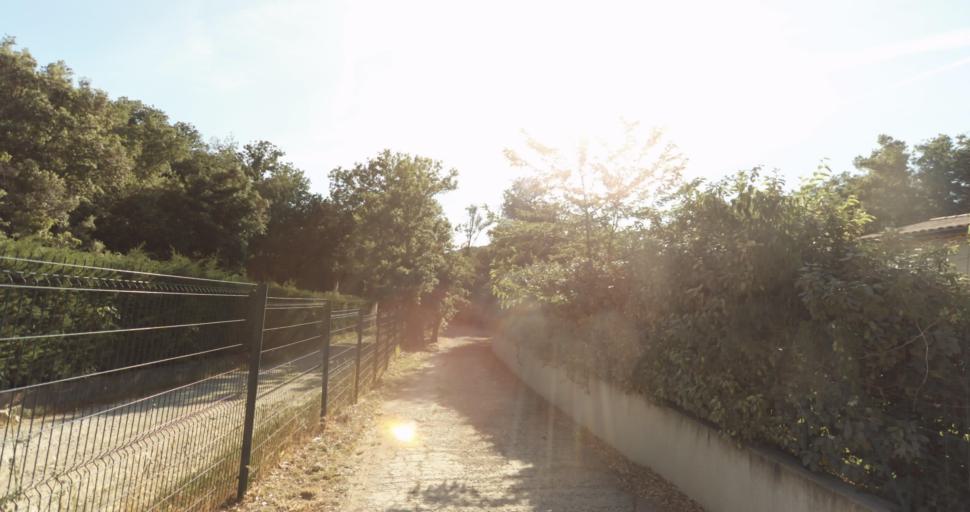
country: FR
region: Provence-Alpes-Cote d'Azur
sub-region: Departement du Var
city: Gassin
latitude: 43.2243
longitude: 6.5721
